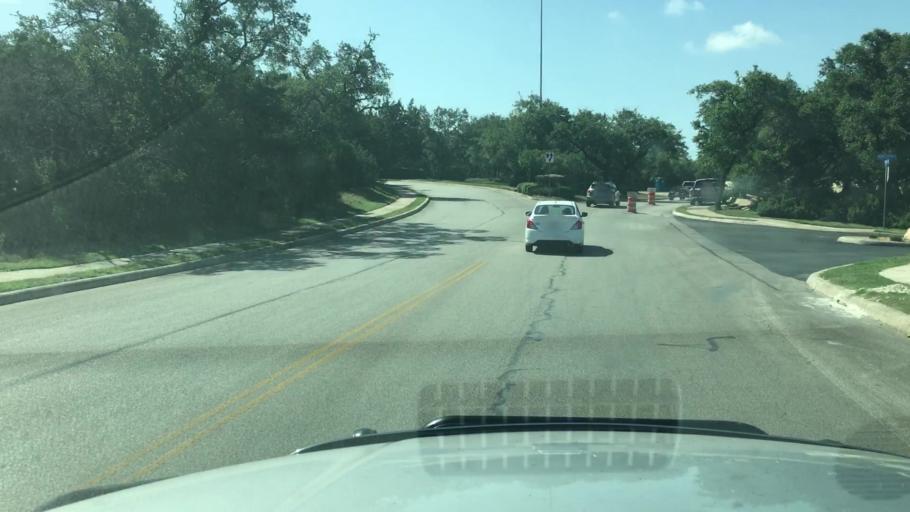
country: US
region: Texas
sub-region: Bexar County
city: Timberwood Park
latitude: 29.6682
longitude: -98.4520
